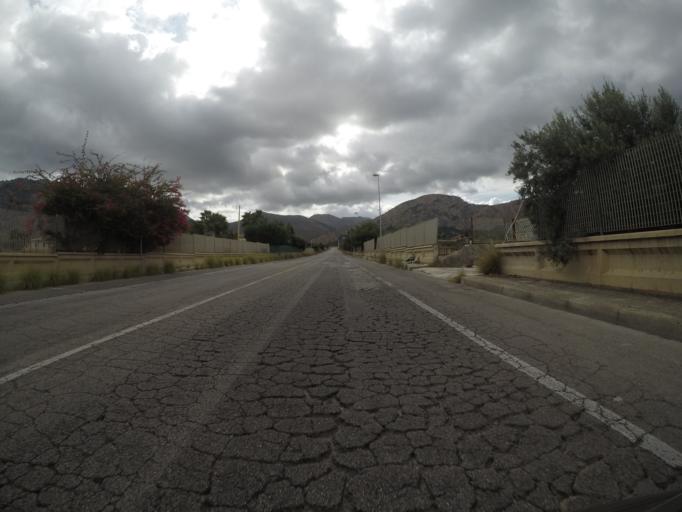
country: IT
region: Sicily
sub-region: Palermo
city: Capaci
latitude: 38.1721
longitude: 13.2195
